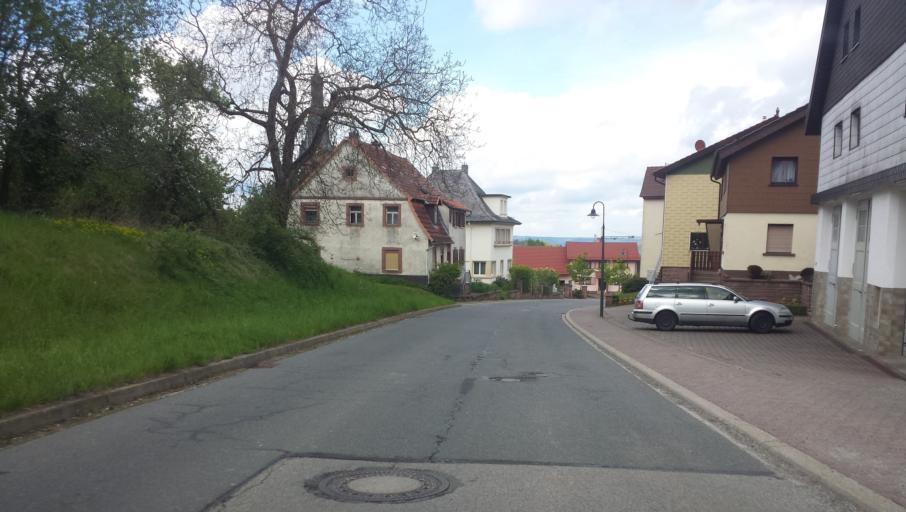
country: DE
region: Baden-Wuerttemberg
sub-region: Karlsruhe Region
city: Zwingenberg
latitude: 49.4624
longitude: 9.0562
